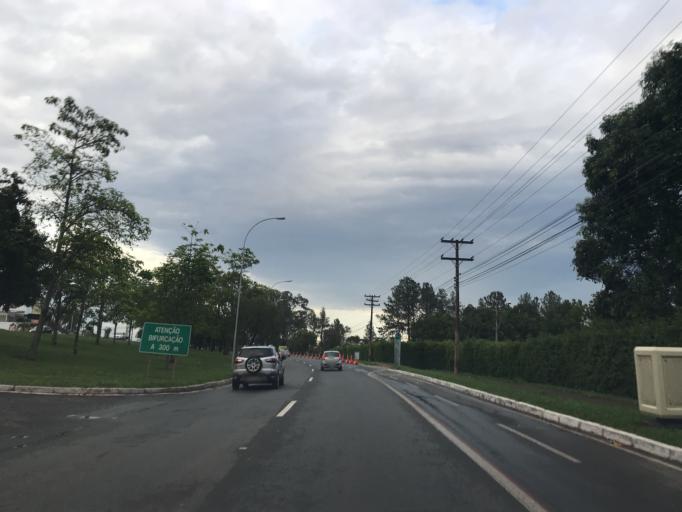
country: BR
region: Federal District
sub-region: Brasilia
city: Brasilia
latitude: -15.8389
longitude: -47.8670
